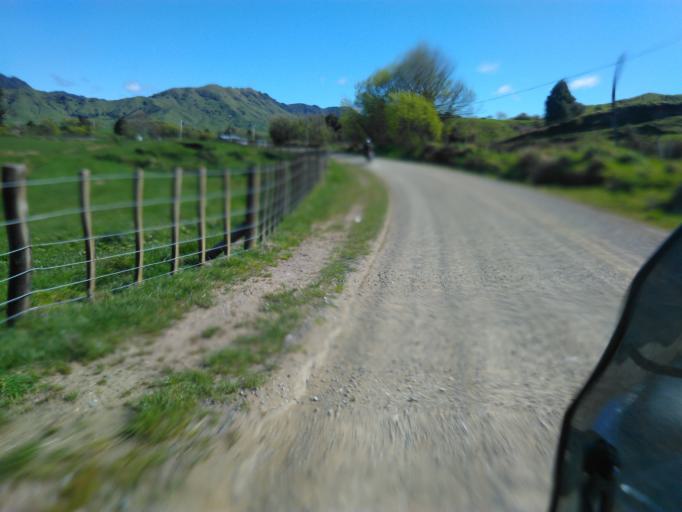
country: NZ
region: Bay of Plenty
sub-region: Opotiki District
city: Opotiki
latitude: -38.2837
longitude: 177.5421
